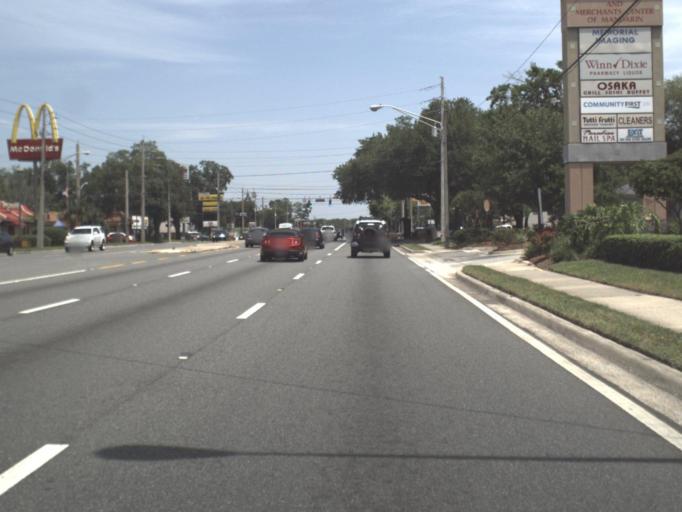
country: US
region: Florida
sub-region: Saint Johns County
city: Fruit Cove
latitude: 30.1595
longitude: -81.6326
